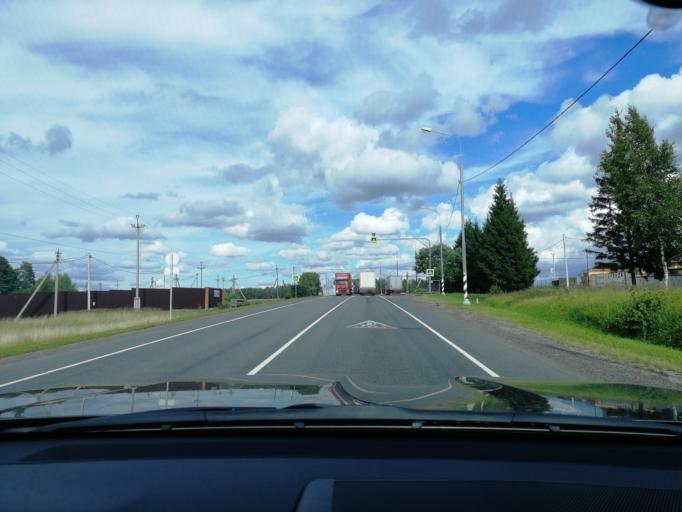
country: RU
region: Moskovskaya
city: Novyy Byt
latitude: 55.0376
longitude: 37.5867
